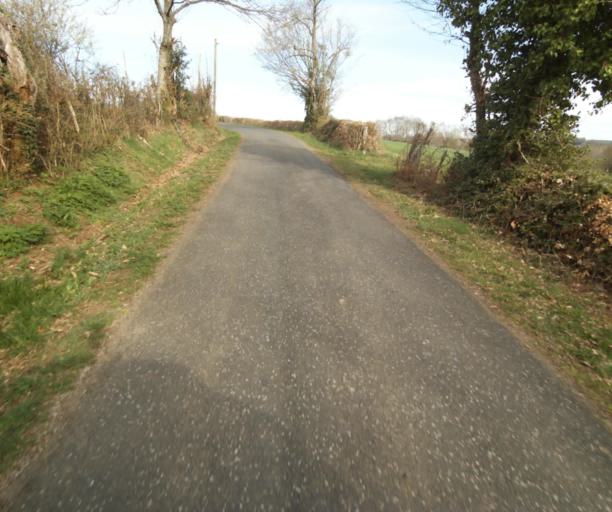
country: FR
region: Limousin
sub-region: Departement de la Correze
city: Chamboulive
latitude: 45.4144
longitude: 1.7852
